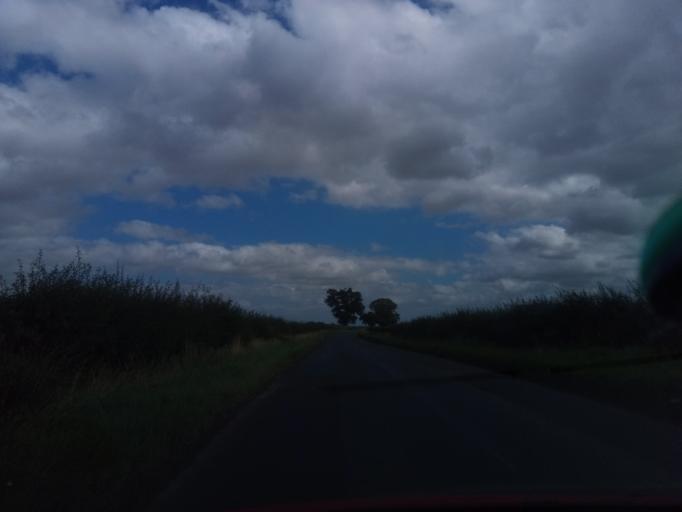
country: GB
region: Scotland
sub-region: The Scottish Borders
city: Kelso
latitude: 55.6232
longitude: -2.3598
